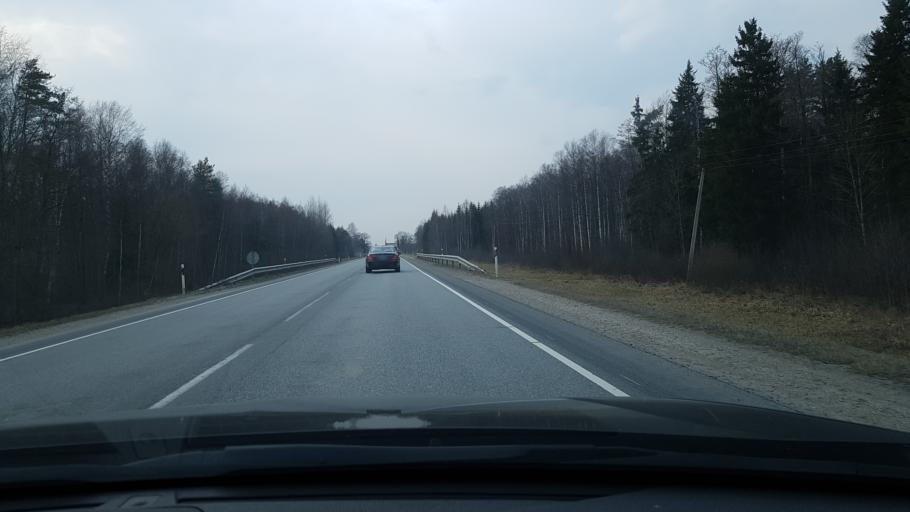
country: EE
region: Tartu
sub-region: Noo vald
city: Noo
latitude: 58.4190
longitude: 26.5278
